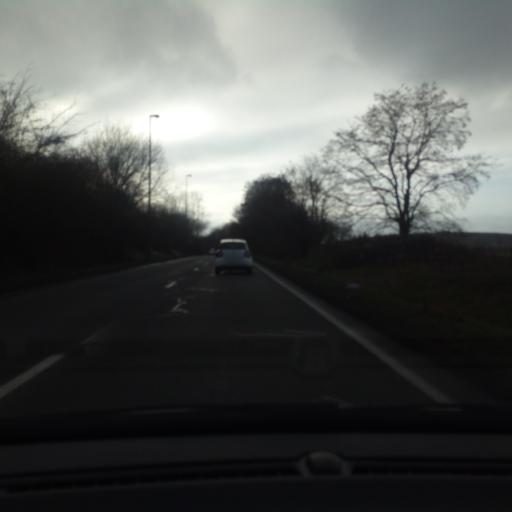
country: BE
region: Wallonia
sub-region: Province du Hainaut
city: Colfontaine
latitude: 50.4245
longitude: 3.8357
